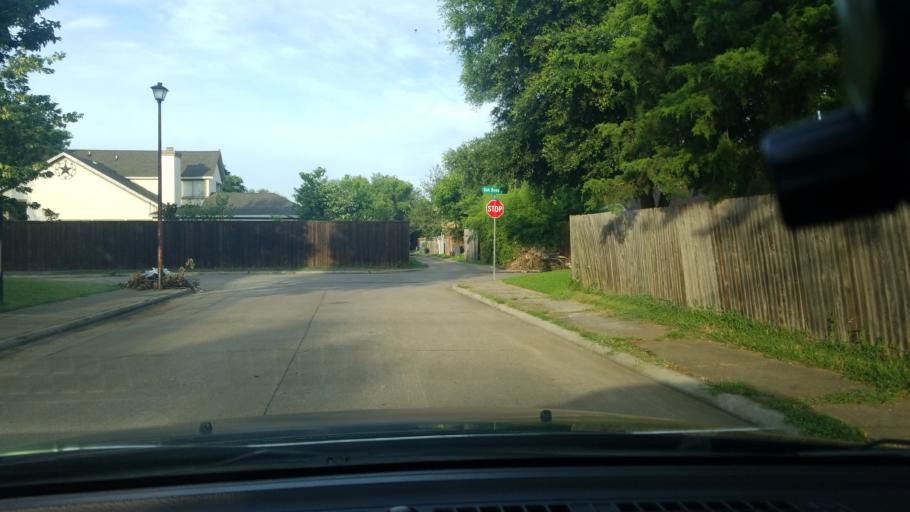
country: US
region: Texas
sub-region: Dallas County
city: Balch Springs
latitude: 32.7564
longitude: -96.6403
